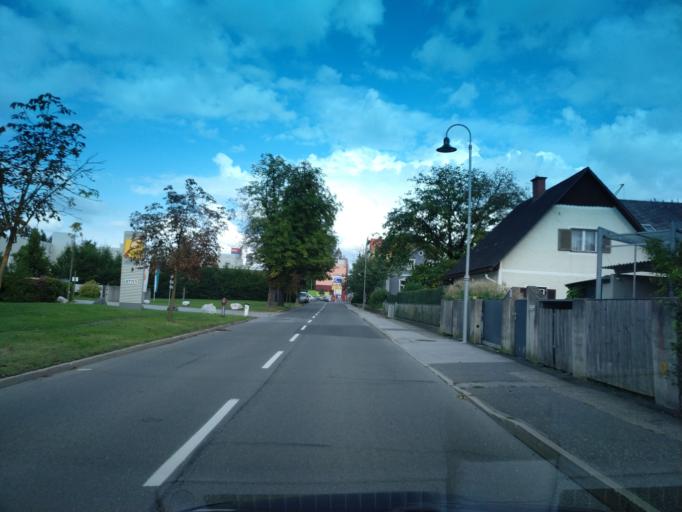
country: AT
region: Styria
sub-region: Politischer Bezirk Leibnitz
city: Leibnitz
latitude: 46.7801
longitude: 15.5330
